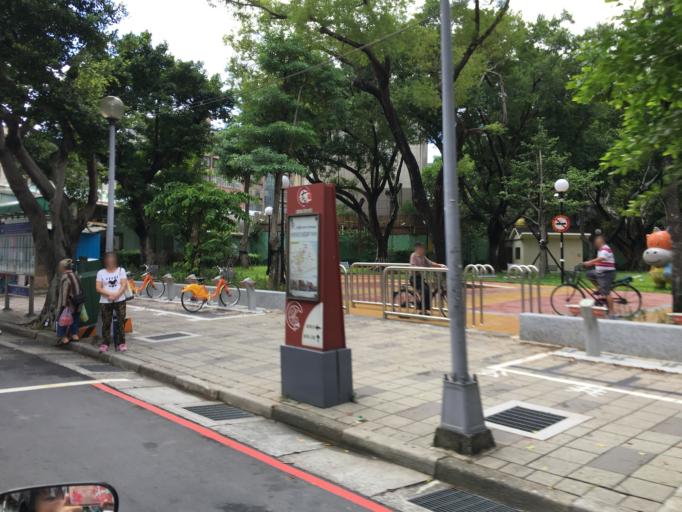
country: TW
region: Taipei
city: Taipei
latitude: 25.0839
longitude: 121.4876
